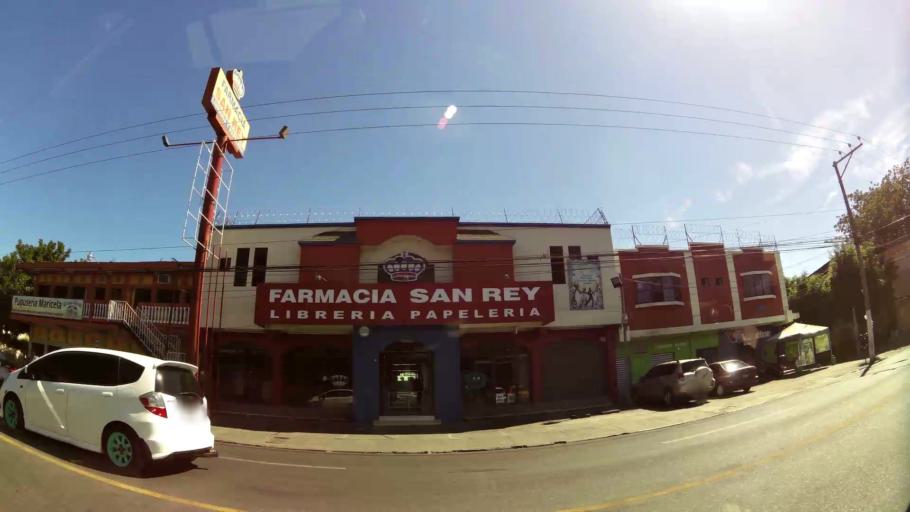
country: SV
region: San Miguel
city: San Miguel
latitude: 13.4915
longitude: -88.1717
